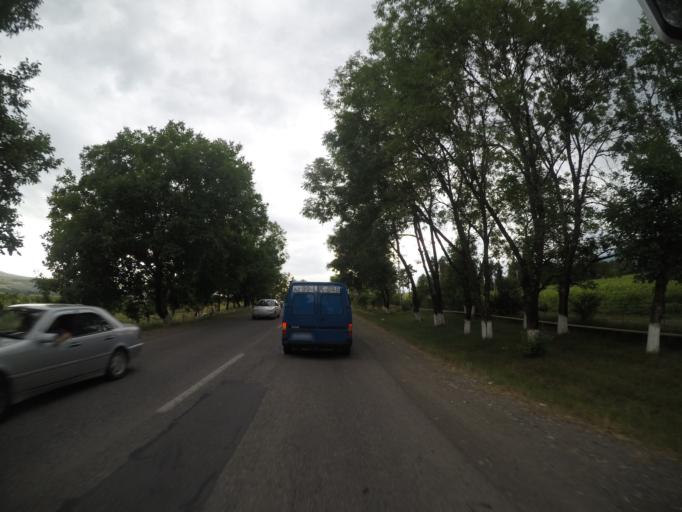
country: AZ
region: Ismayilli
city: Ismayilli
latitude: 40.7764
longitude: 48.1951
